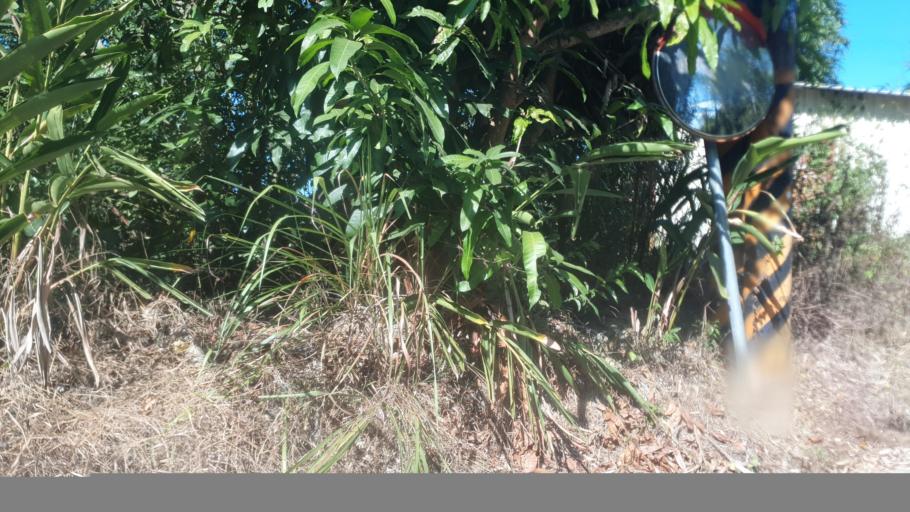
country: TW
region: Taiwan
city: Yujing
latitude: 23.0283
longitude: 120.3939
